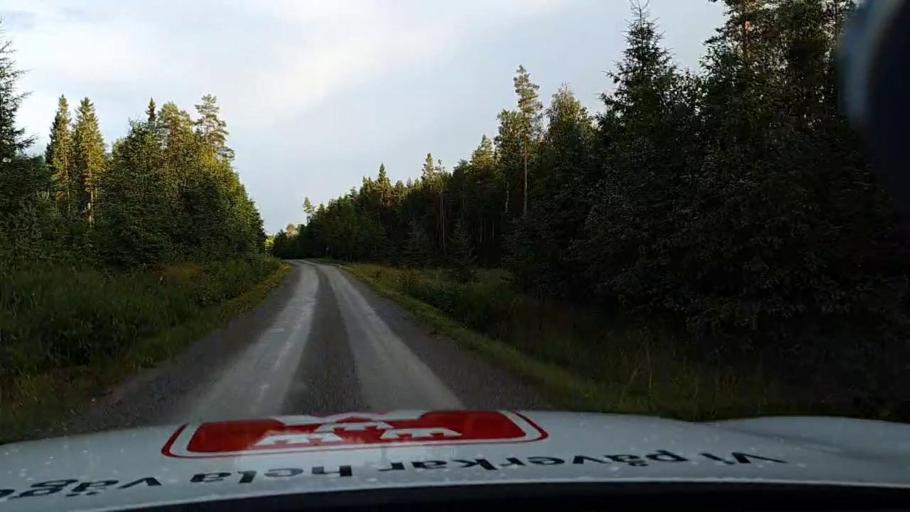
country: SE
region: Jaemtland
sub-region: Bergs Kommun
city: Hoverberg
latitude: 62.8590
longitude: 14.5336
